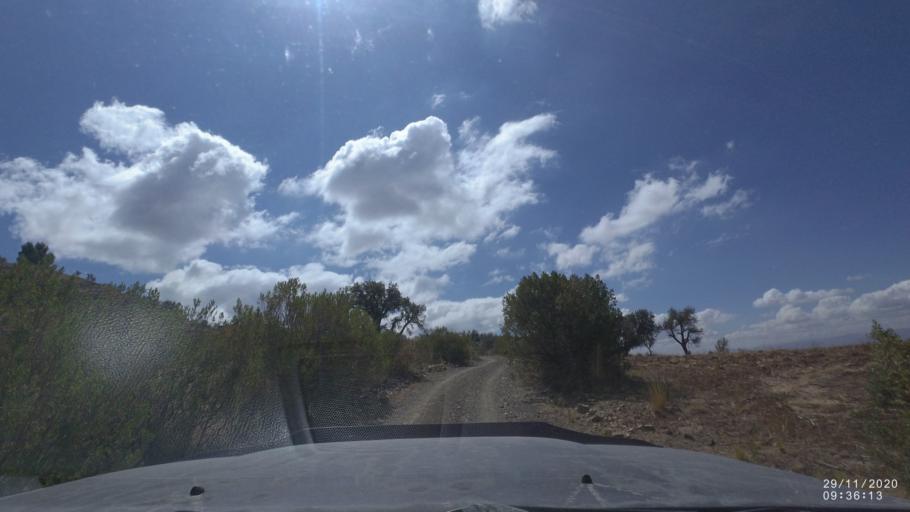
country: BO
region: Cochabamba
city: Cochabamba
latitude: -17.3095
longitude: -66.1882
